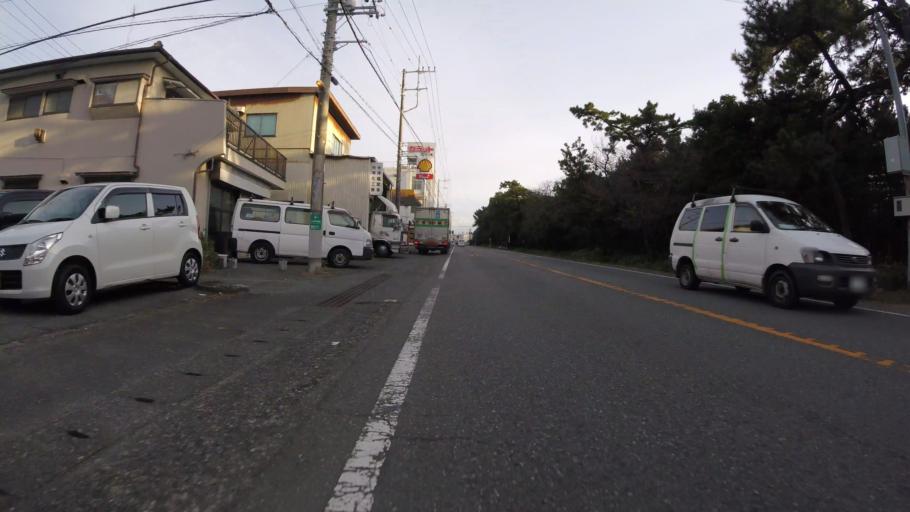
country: JP
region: Shizuoka
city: Numazu
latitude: 35.1045
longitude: 138.8373
